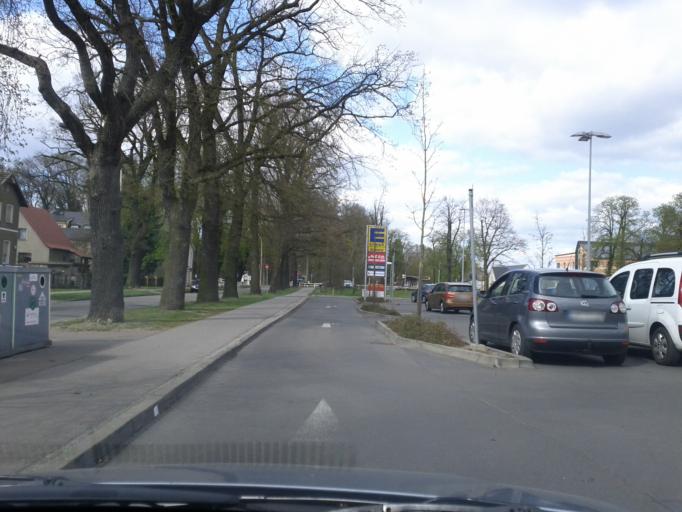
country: DE
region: Brandenburg
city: Schoneiche
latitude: 52.4776
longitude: 13.6998
